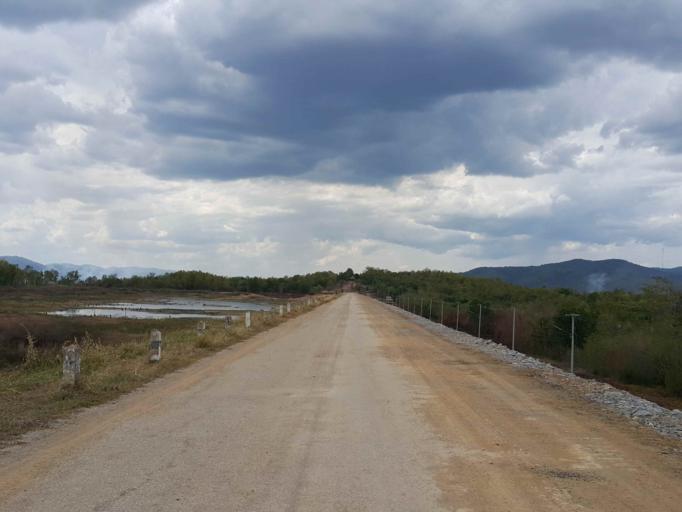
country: TH
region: Sukhothai
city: Thung Saliam
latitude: 17.3201
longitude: 99.4235
